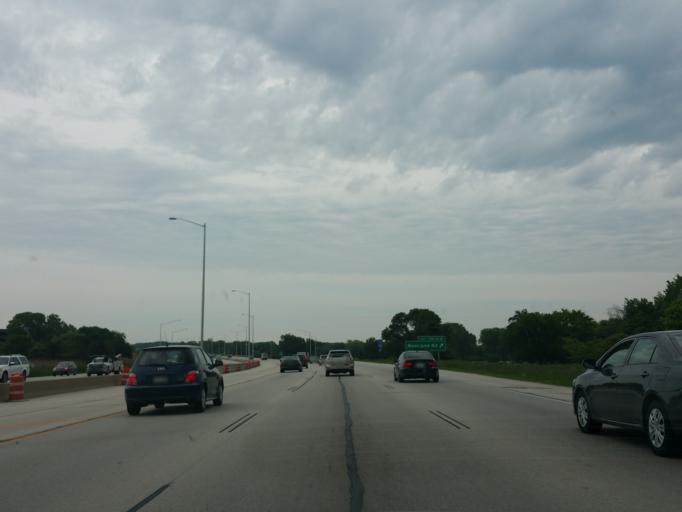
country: US
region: Wisconsin
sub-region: Waukesha County
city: Brookfield
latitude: 43.0253
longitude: -88.1169
